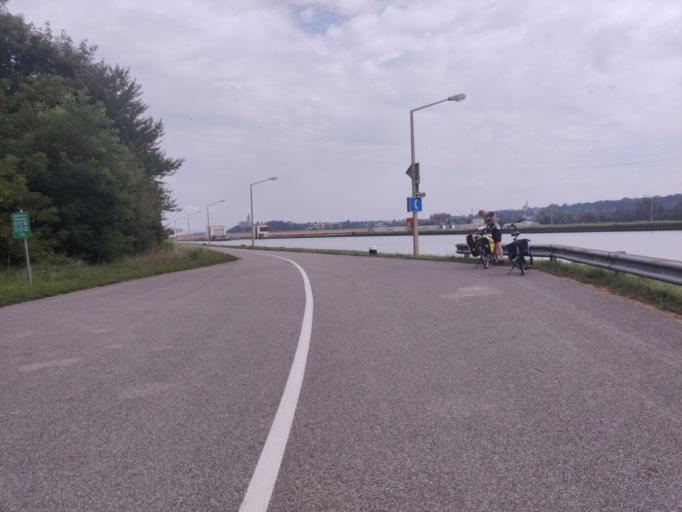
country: AT
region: Lower Austria
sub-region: Politischer Bezirk Amstetten
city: Strengberg
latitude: 48.1681
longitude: 14.6854
